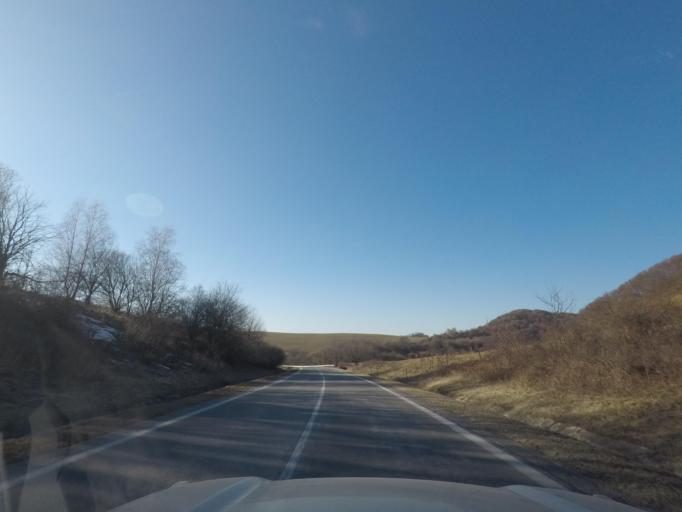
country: SK
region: Presovsky
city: Medzilaborce
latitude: 49.2341
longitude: 21.9551
